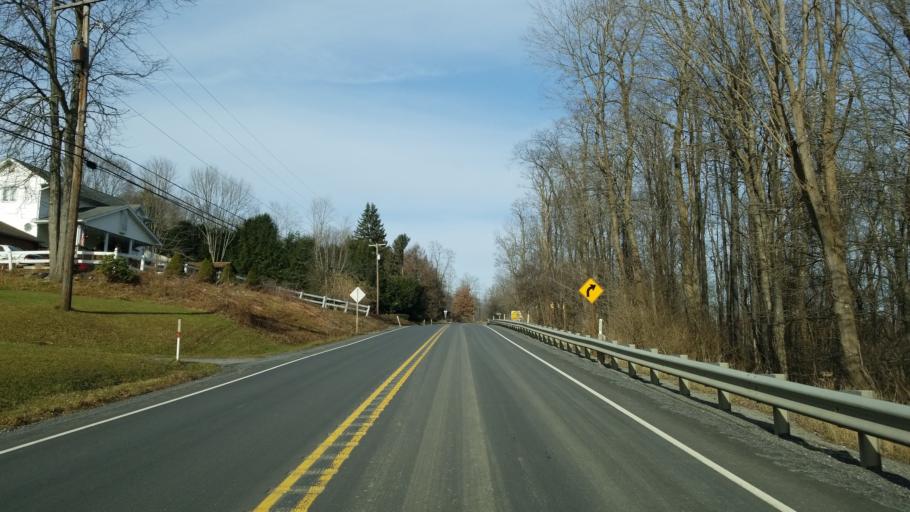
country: US
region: Pennsylvania
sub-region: Clearfield County
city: Curwensville
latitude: 40.9587
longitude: -78.6119
